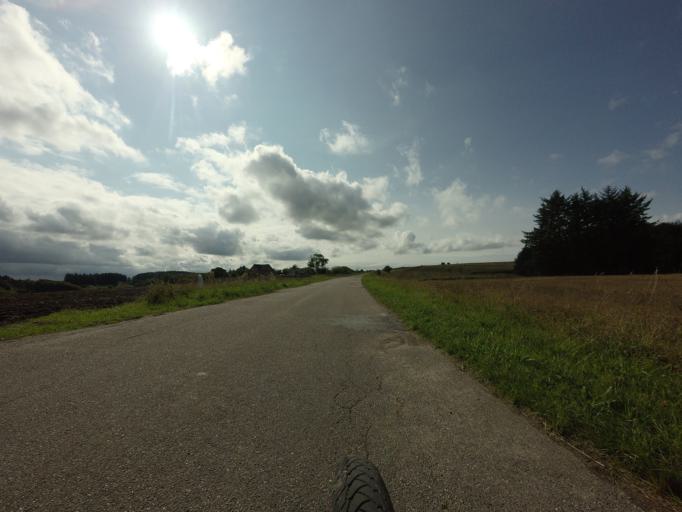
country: DK
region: North Denmark
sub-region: Hjorring Kommune
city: Hjorring
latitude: 57.5373
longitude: 10.0556
